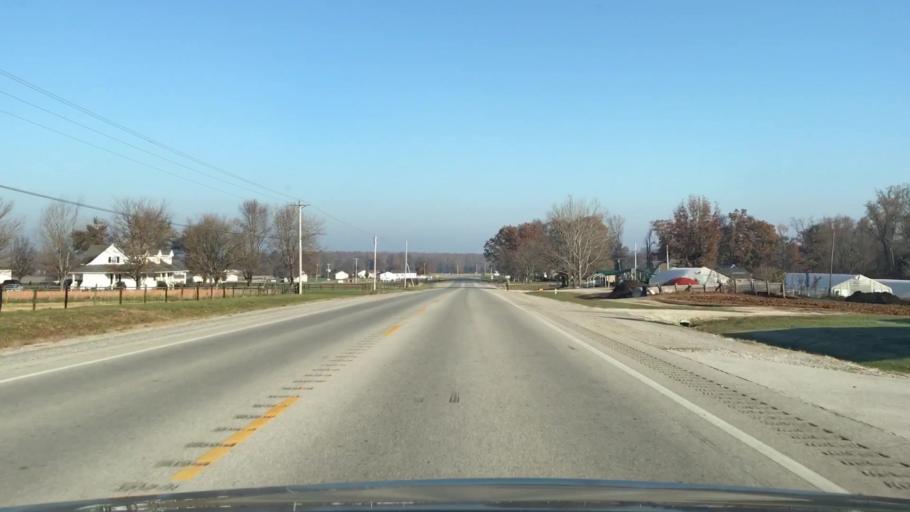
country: US
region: Kentucky
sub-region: Edmonson County
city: Brownsville
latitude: 37.1098
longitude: -86.2293
